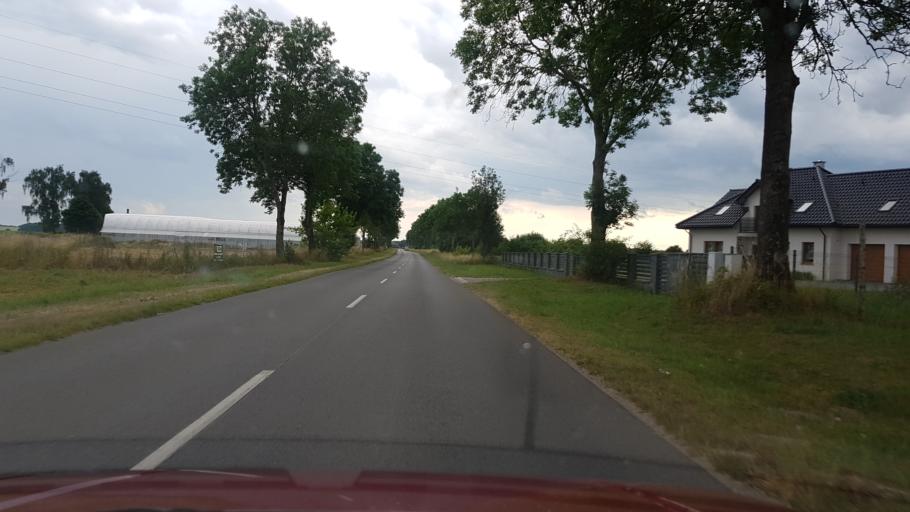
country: PL
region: West Pomeranian Voivodeship
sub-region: Powiat gryficki
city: Gryfice
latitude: 53.8975
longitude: 15.1802
